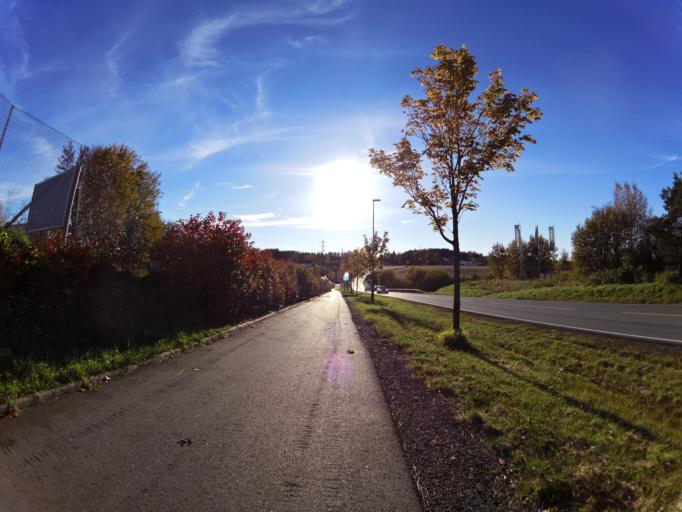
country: NO
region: Ostfold
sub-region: Sarpsborg
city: Sarpsborg
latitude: 59.2624
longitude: 11.1155
